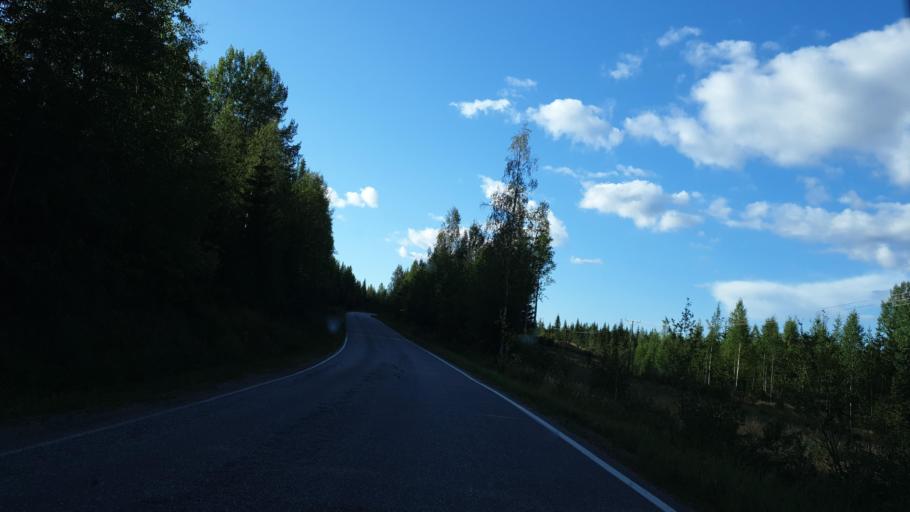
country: FI
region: Northern Savo
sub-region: Koillis-Savo
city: Kaavi
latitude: 63.0326
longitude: 28.6085
